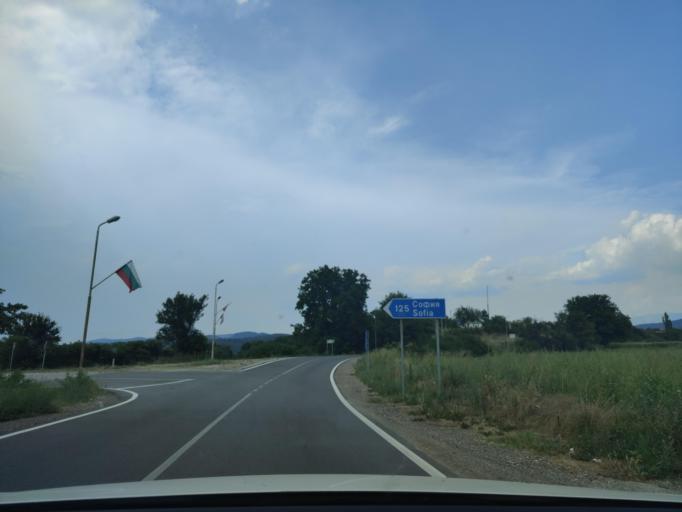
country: BG
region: Blagoevgrad
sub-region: Obshtina Simitli
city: Simitli
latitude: 41.8537
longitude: 23.1380
